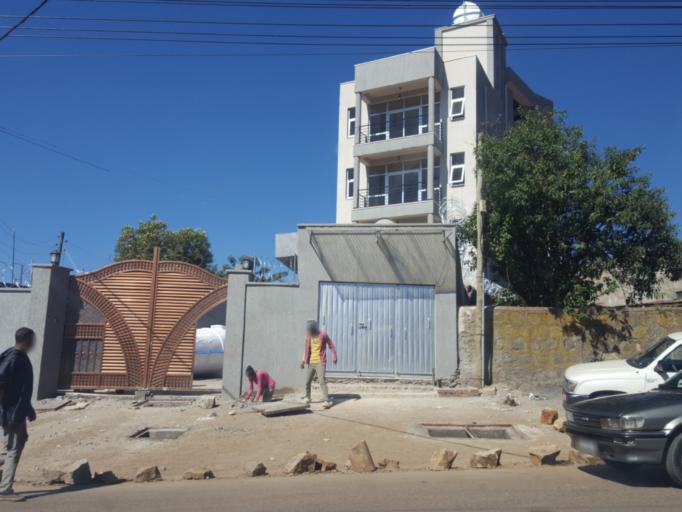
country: ET
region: Adis Abeba
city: Addis Ababa
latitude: 9.0582
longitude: 38.7441
